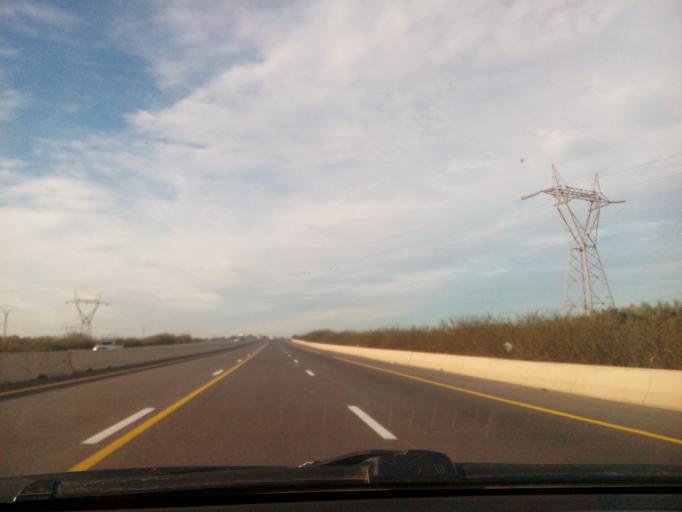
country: DZ
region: Mascara
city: Sig
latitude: 35.5785
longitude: -0.2565
